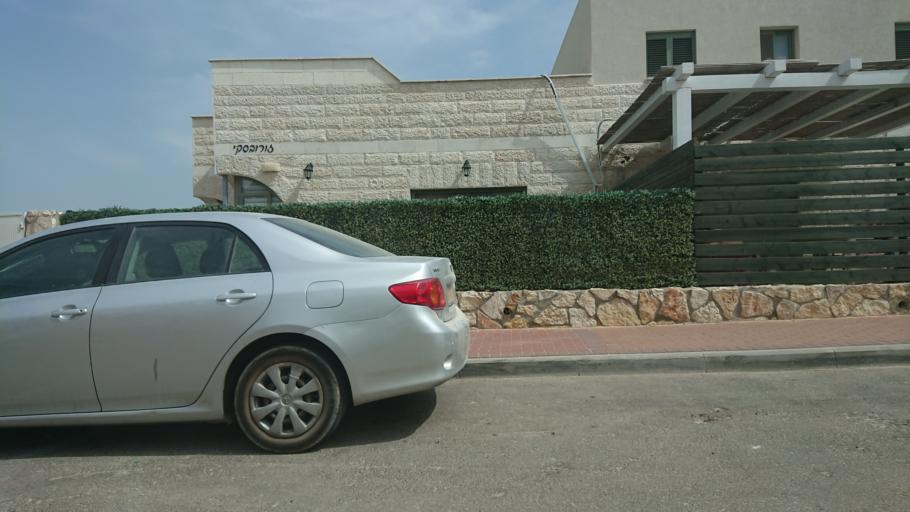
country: PS
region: West Bank
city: Rafat
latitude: 32.0633
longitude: 35.0552
